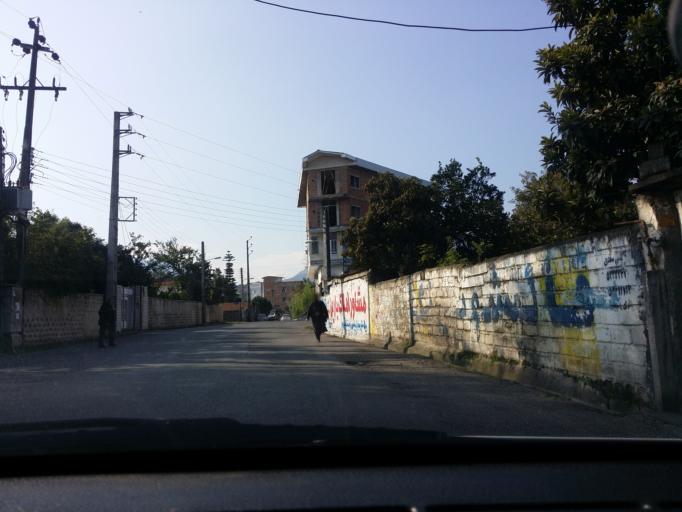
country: IR
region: Mazandaran
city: Chalus
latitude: 36.6544
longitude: 51.4151
